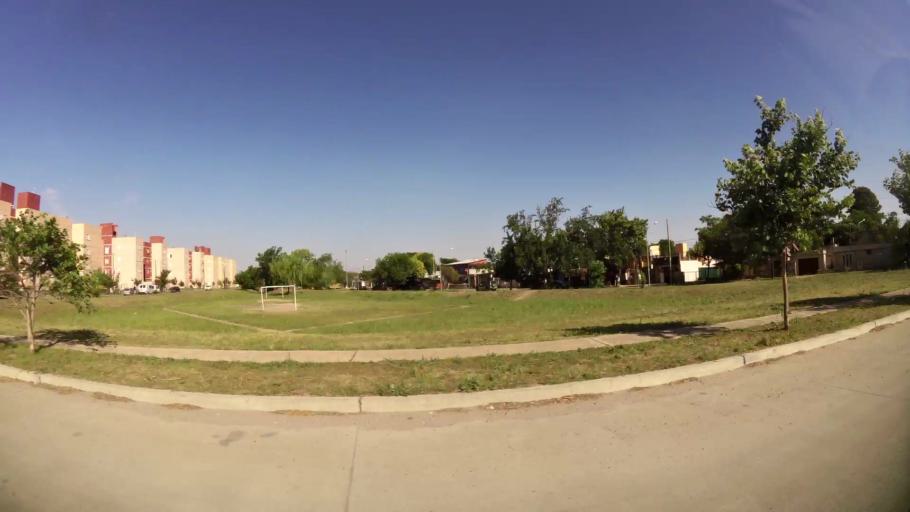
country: AR
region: Cordoba
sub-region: Departamento de Capital
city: Cordoba
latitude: -31.3570
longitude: -64.1913
